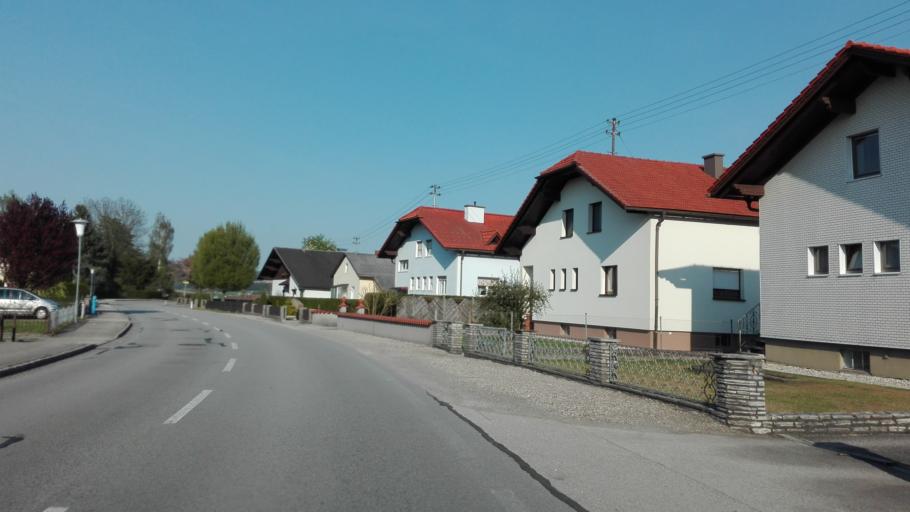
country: AT
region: Upper Austria
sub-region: Politischer Bezirk Grieskirchen
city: Grieskirchen
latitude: 48.3354
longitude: 13.8448
